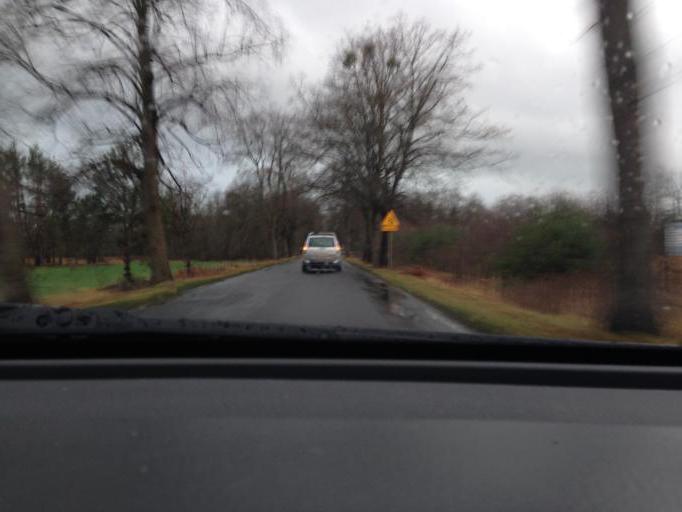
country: PL
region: Opole Voivodeship
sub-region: Powiat opolski
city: Wegry
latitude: 50.7236
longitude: 18.0221
